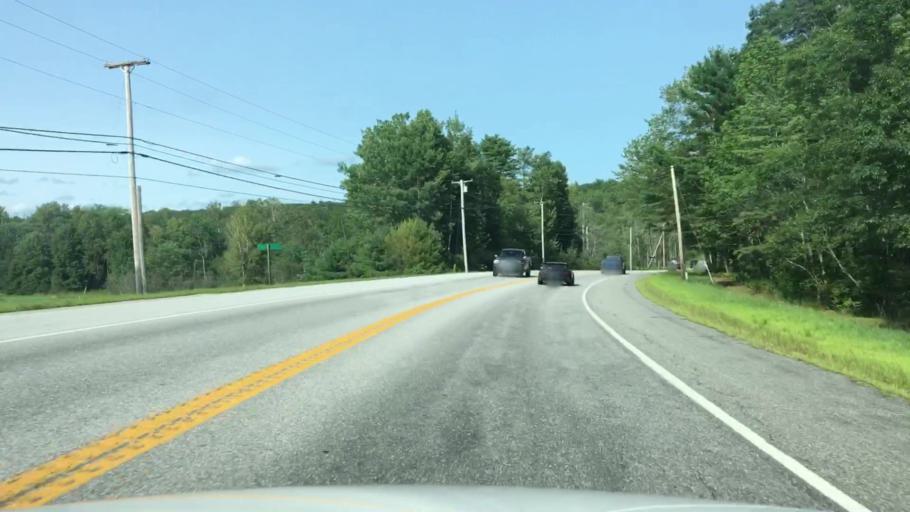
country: US
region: Maine
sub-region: Lincoln County
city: Nobleboro
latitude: 44.0928
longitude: -69.4684
